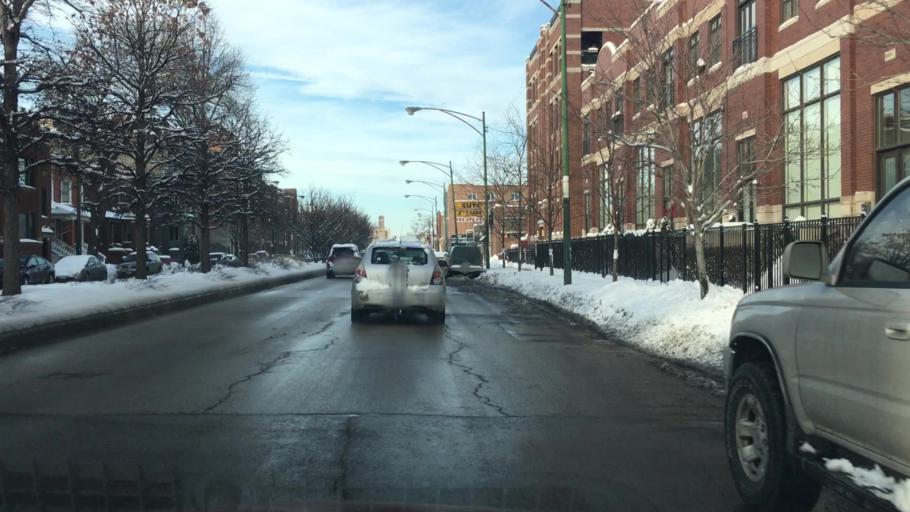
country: US
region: Illinois
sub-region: Cook County
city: Chicago
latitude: 41.9300
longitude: -87.6682
